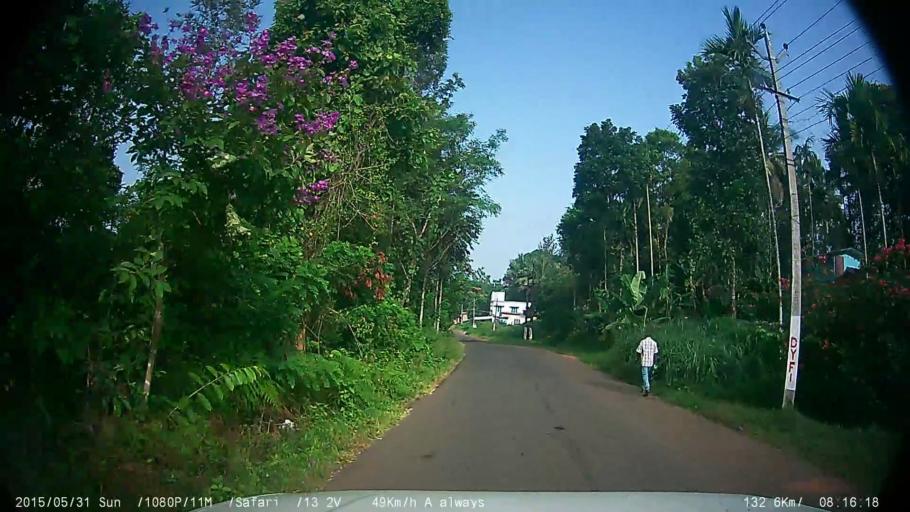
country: IN
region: Kerala
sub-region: Wayanad
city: Kalpetta
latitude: 11.6544
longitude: 75.9975
